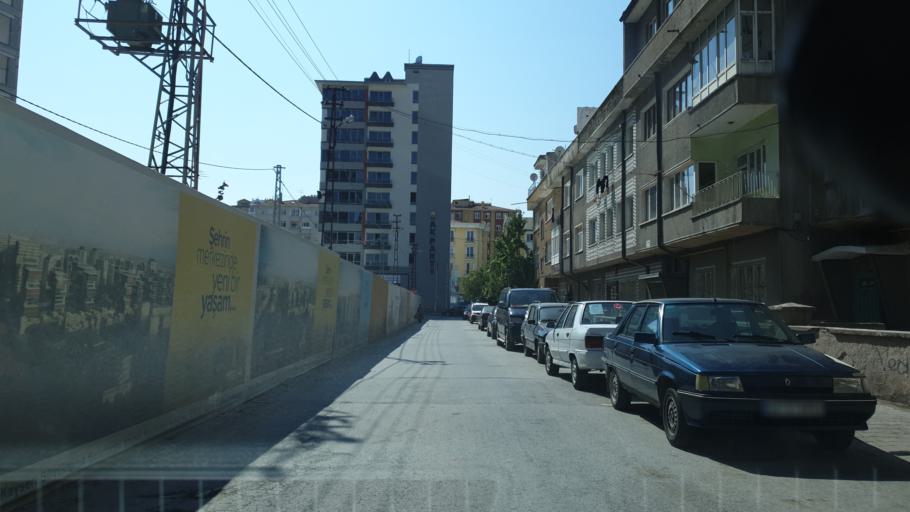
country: TR
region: Kayseri
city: Kayseri
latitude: 38.7274
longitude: 35.4901
